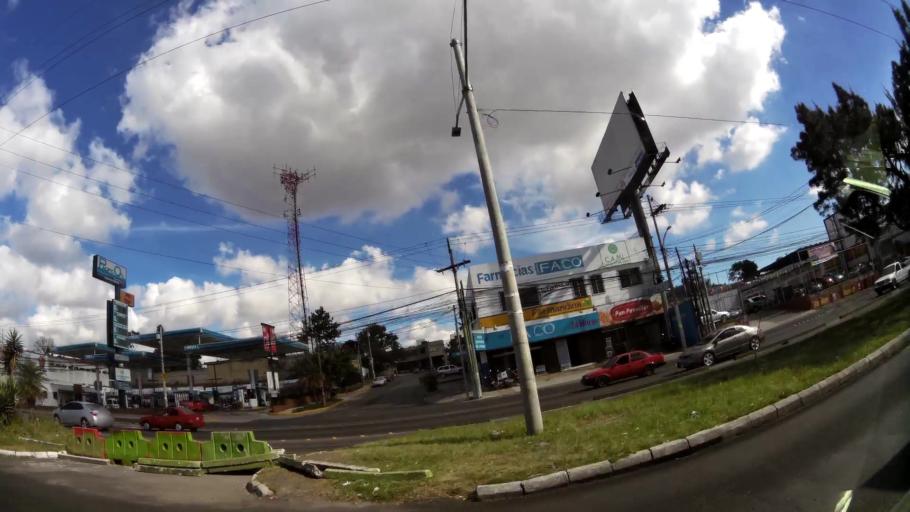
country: GT
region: Guatemala
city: Villa Nueva
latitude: 14.5795
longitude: -90.5686
